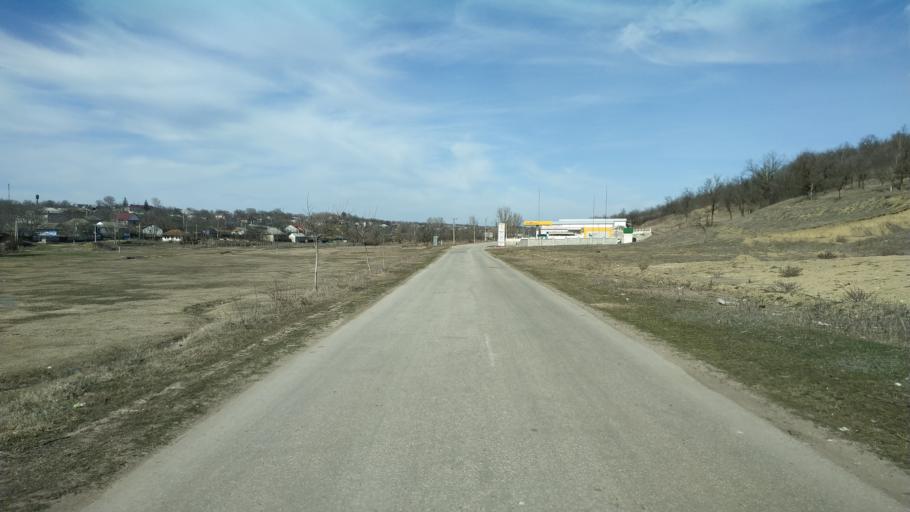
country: MD
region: Nisporeni
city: Nisporeni
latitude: 46.9589
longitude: 28.2193
